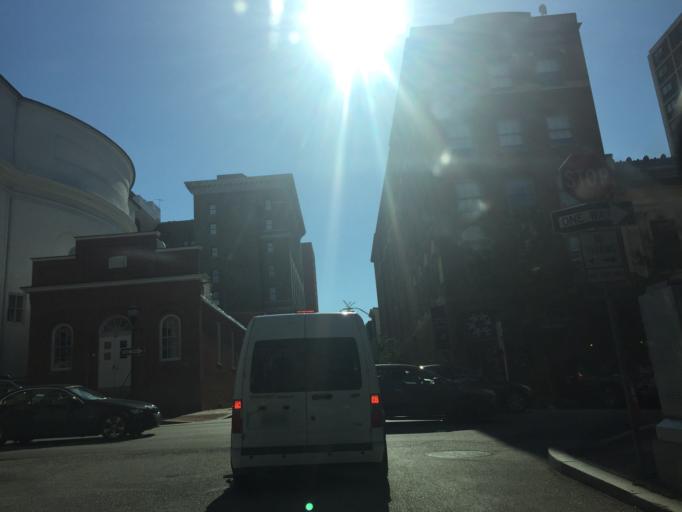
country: US
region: Maryland
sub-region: City of Baltimore
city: Baltimore
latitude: 39.2957
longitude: -76.6154
